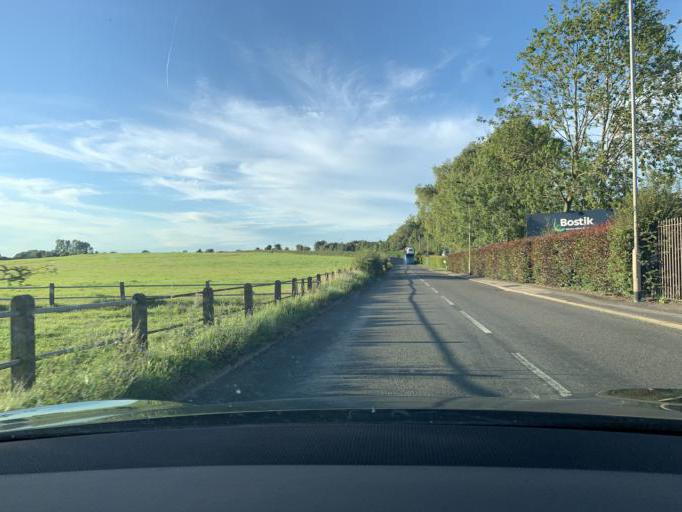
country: GB
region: England
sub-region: Staffordshire
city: Stafford
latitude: 52.8276
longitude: -2.1168
